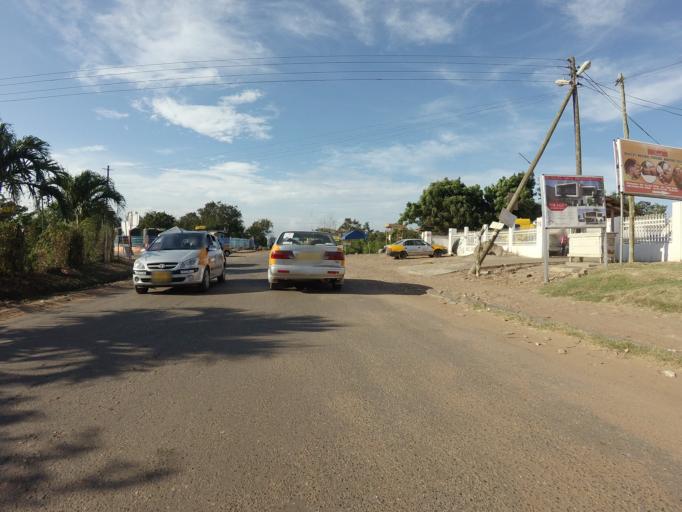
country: GH
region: Greater Accra
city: Tema
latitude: 5.6521
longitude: -0.0643
